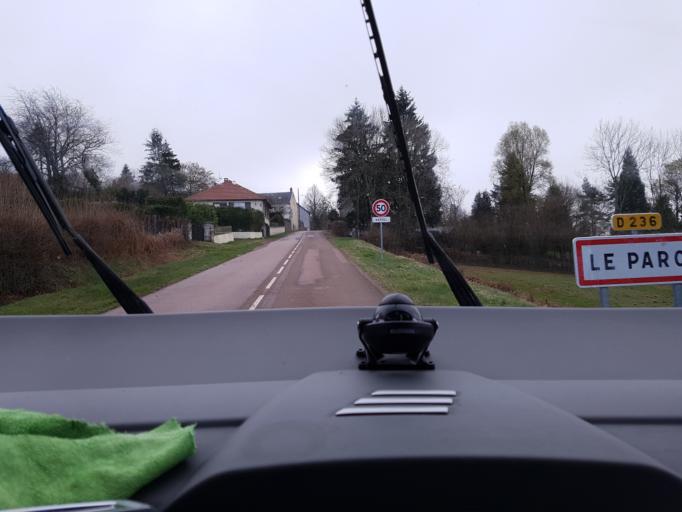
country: FR
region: Bourgogne
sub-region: Departement de la Cote-d'Or
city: Saulieu
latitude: 47.2716
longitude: 4.0292
